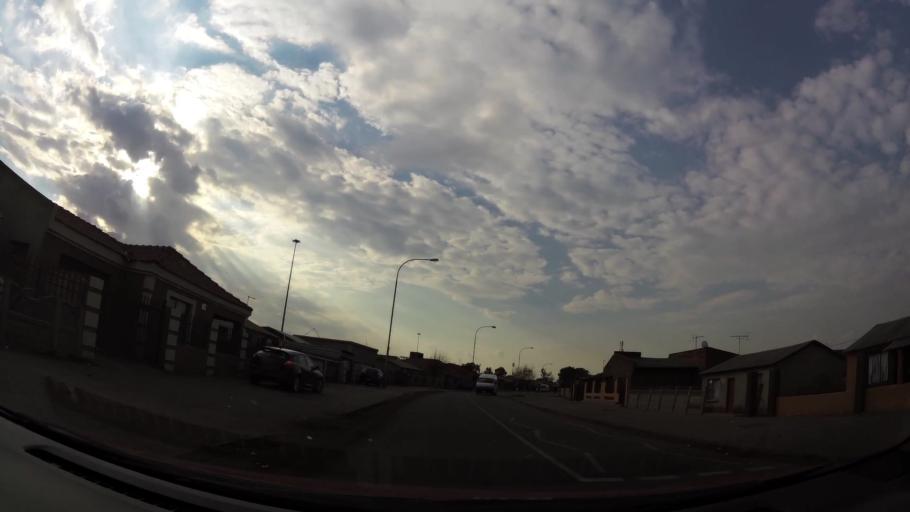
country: ZA
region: Gauteng
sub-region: Sedibeng District Municipality
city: Vanderbijlpark
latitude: -26.6956
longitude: 27.8658
